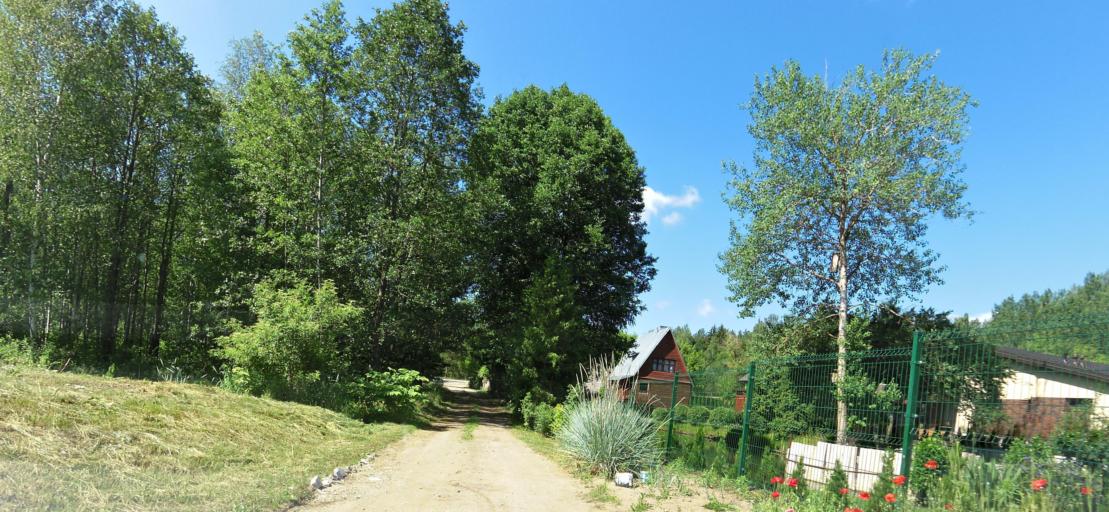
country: LT
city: Nemencine
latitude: 54.7975
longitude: 25.3979
